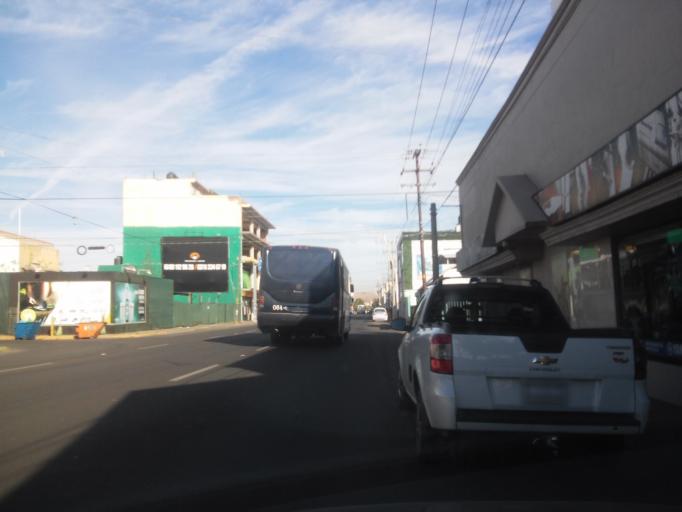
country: MX
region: Durango
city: Victoria de Durango
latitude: 24.0300
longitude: -104.6533
